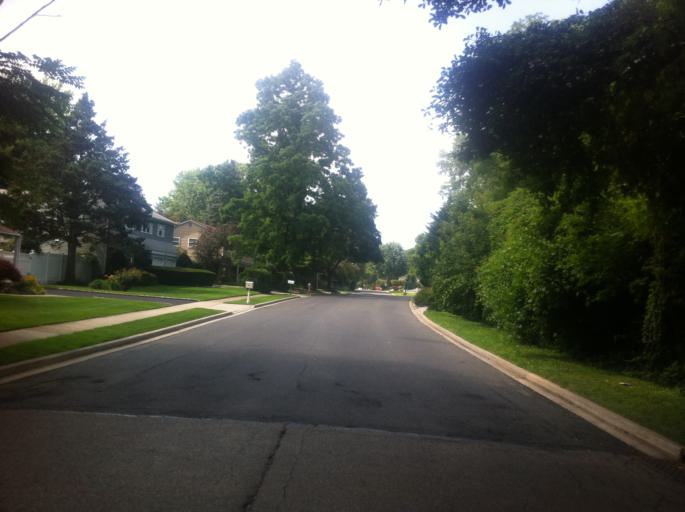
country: US
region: New York
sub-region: Nassau County
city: Locust Valley
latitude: 40.8547
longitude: -73.5986
